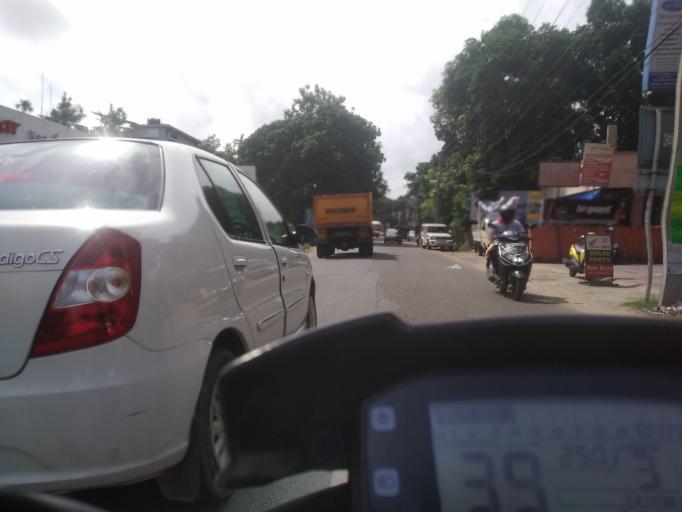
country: IN
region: Kerala
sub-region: Thrissur District
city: Kodungallur
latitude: 10.1413
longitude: 76.2293
